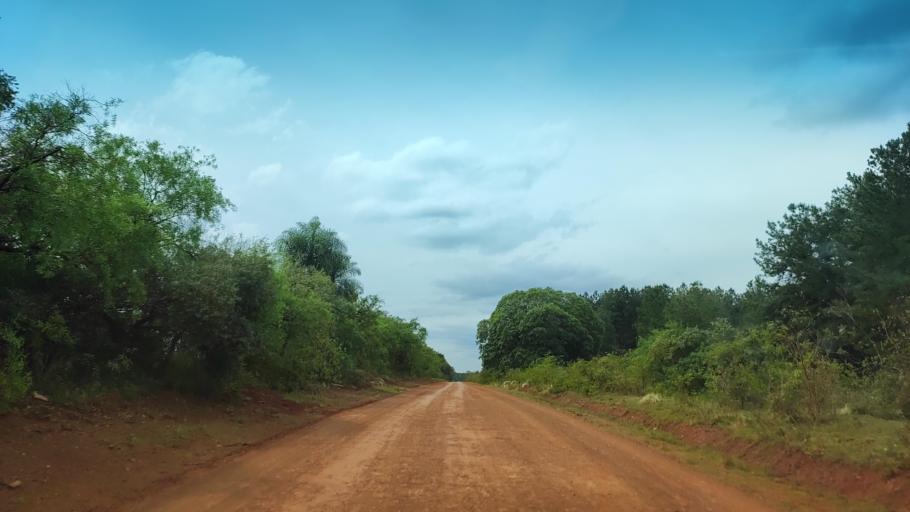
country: AR
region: Misiones
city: Garupa
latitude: -27.5131
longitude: -55.9706
